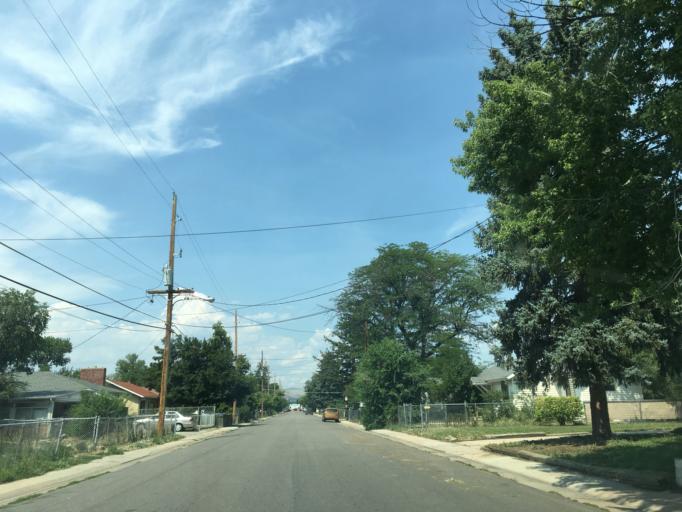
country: US
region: Colorado
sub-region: Jefferson County
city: Lakewood
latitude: 39.6976
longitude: -105.0447
